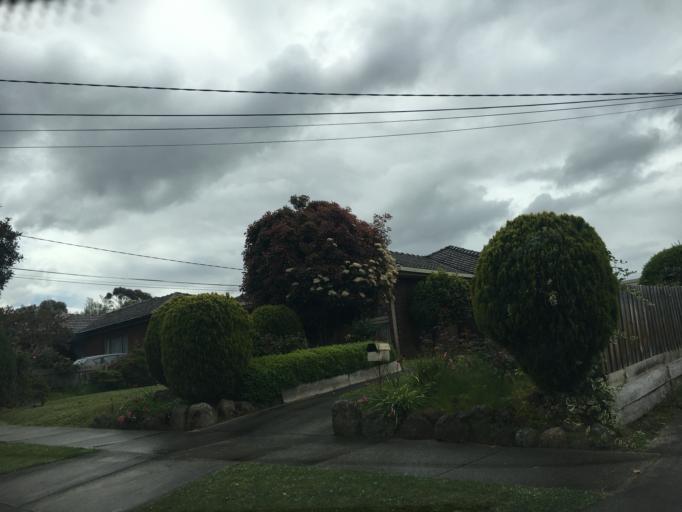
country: AU
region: Victoria
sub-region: Whitehorse
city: Vermont South
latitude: -37.8666
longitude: 145.1635
